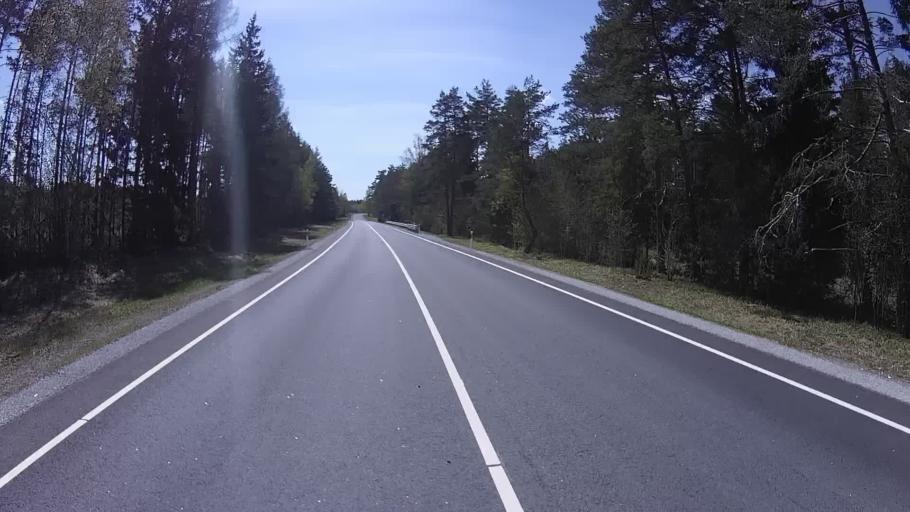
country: EE
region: Laeaene
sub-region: Ridala Parish
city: Uuemoisa
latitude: 59.0404
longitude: 23.8303
